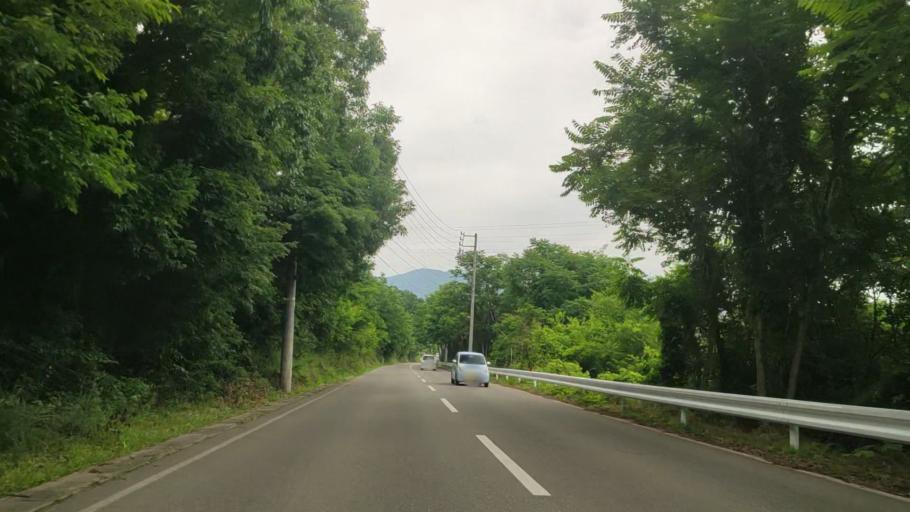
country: JP
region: Nagano
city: Kamimaruko
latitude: 36.3202
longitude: 138.3354
